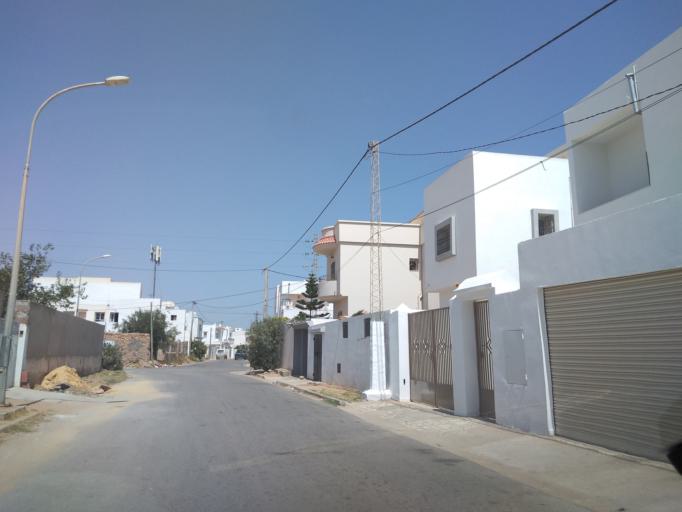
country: TN
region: Safaqis
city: Sfax
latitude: 34.7554
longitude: 10.7402
